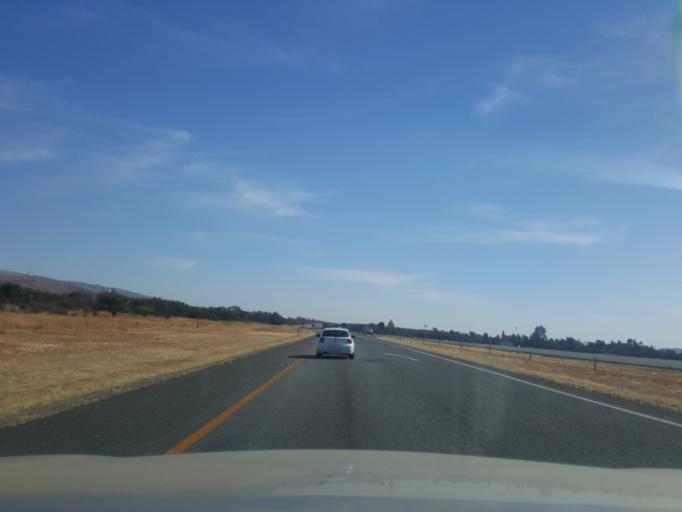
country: ZA
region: North-West
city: Ga-Rankuwa
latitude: -25.6557
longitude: 28.0356
